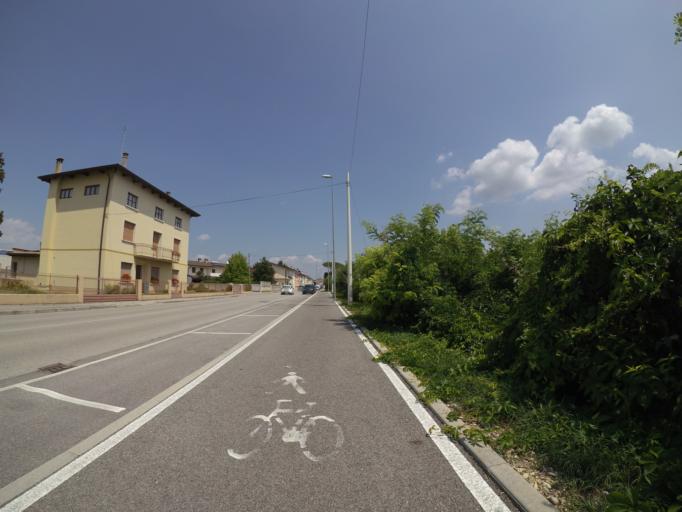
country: IT
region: Friuli Venezia Giulia
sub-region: Provincia di Udine
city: Sedegliano
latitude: 46.0097
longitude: 12.9704
